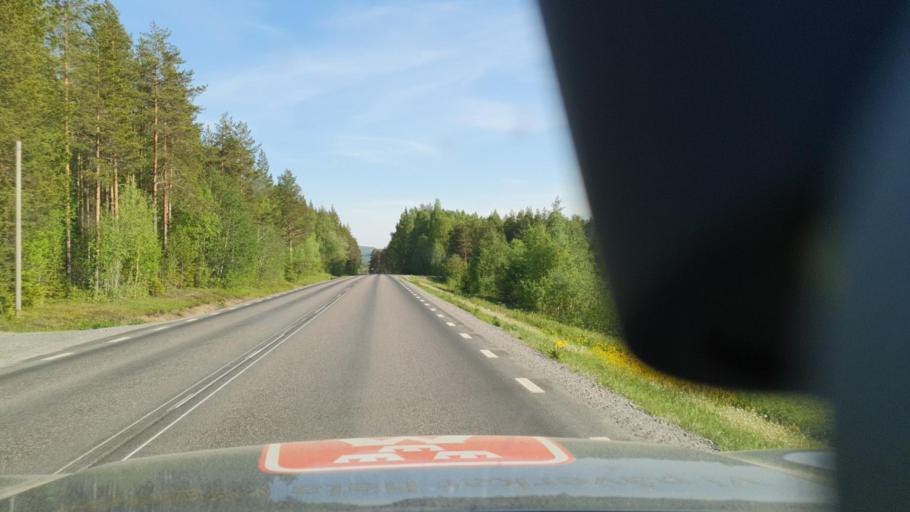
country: SE
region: Norrbotten
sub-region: Bodens Kommun
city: Boden
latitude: 65.8731
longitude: 21.4113
